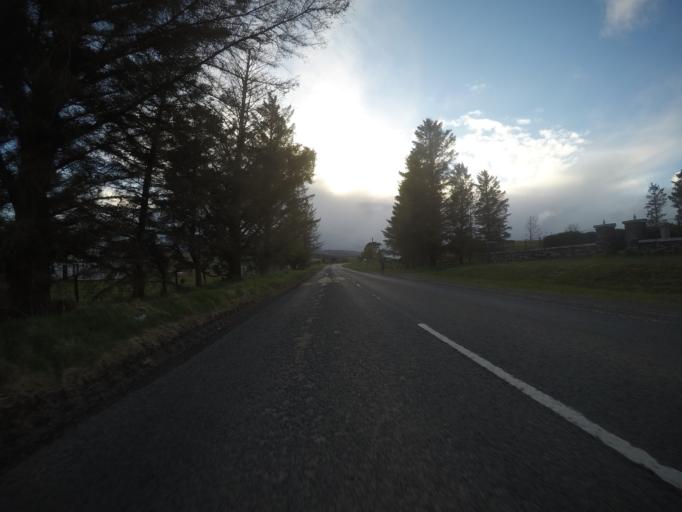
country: GB
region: Scotland
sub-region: Highland
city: Isle of Skye
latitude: 57.4513
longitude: -6.2855
